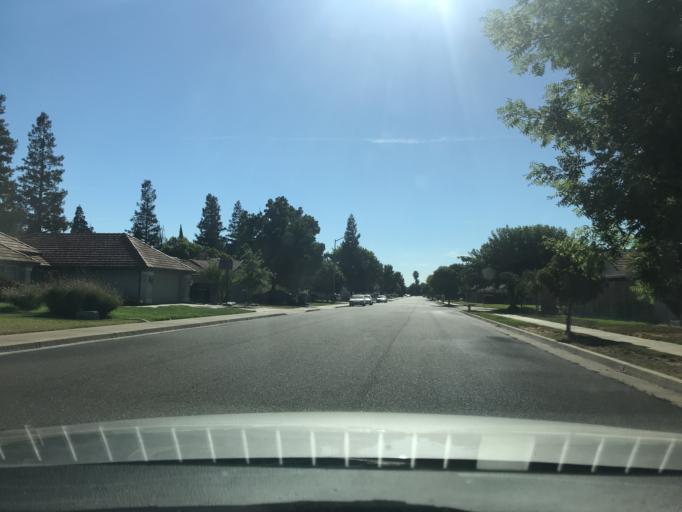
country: US
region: California
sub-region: Merced County
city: Atwater
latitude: 37.3487
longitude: -120.5821
